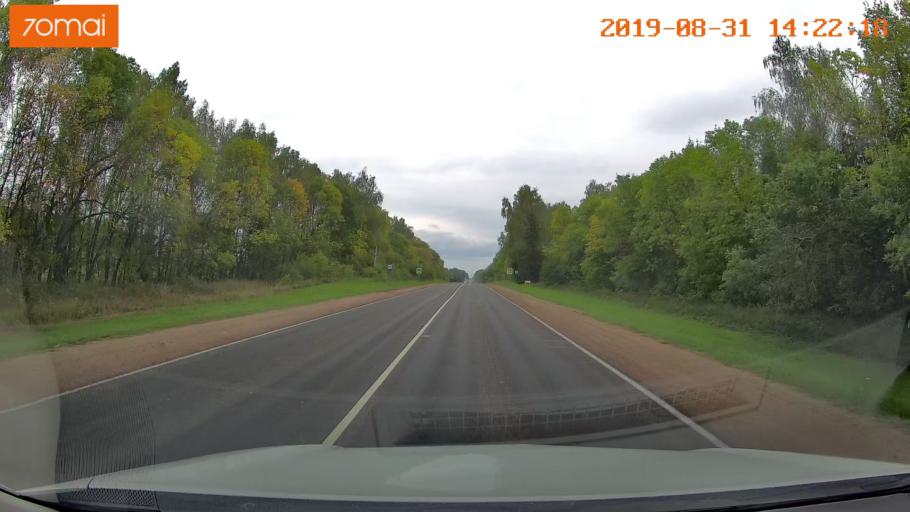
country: RU
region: Smolensk
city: Yekimovichi
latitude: 54.0909
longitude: 33.2153
